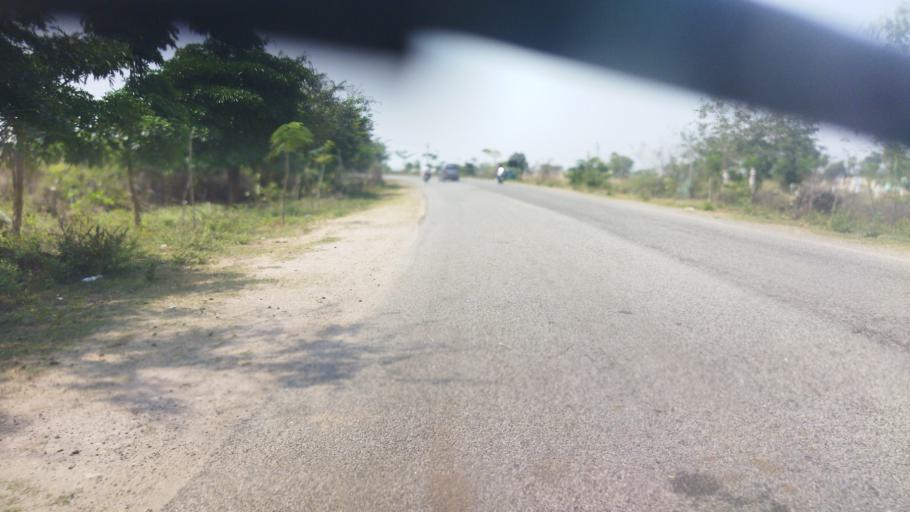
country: IN
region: Telangana
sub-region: Nalgonda
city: Nalgonda
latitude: 17.1227
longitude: 79.2903
